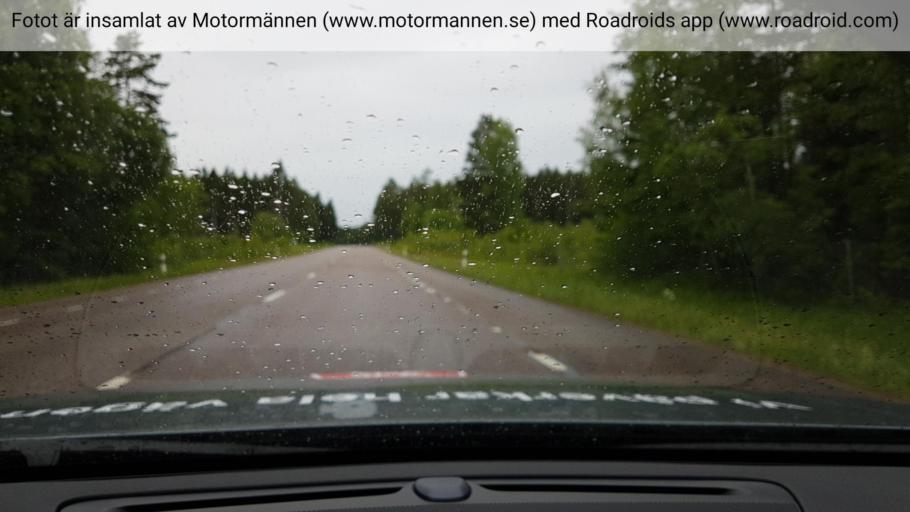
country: SE
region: Uppsala
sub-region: Alvkarleby Kommun
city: AElvkarleby
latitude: 60.5915
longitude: 17.4635
